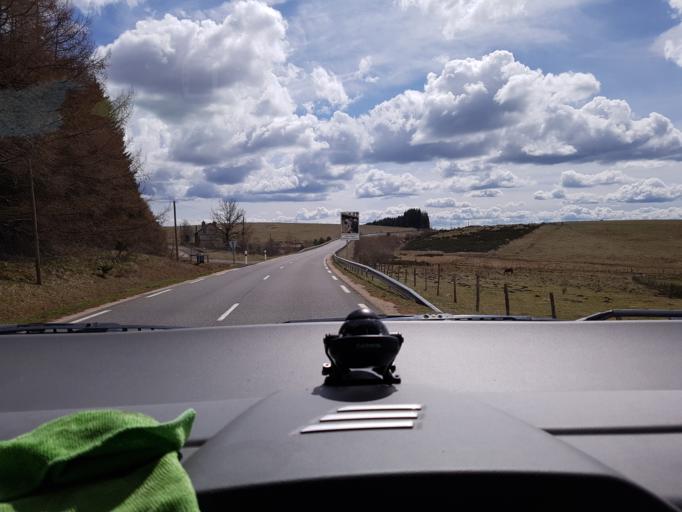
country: FR
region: Midi-Pyrenees
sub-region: Departement de l'Aveyron
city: Laguiole
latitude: 44.7333
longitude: 2.8722
